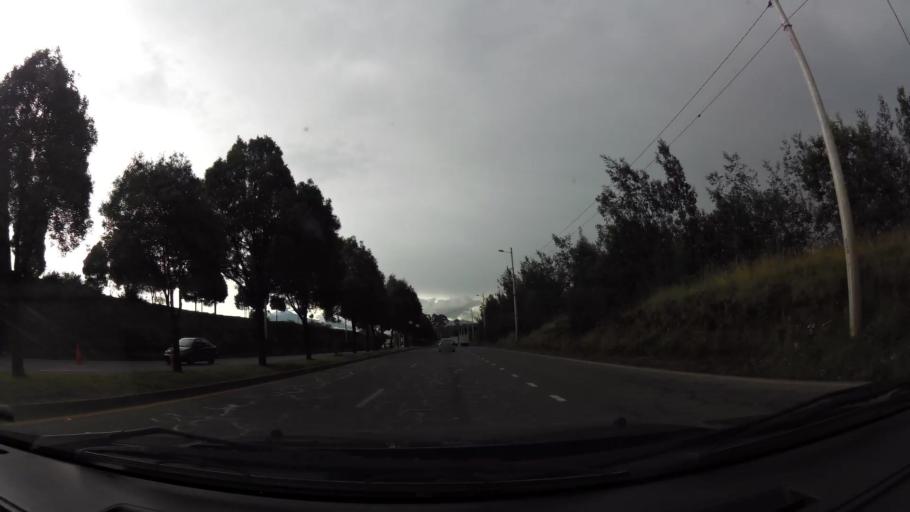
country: EC
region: Pichincha
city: Sangolqui
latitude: -0.3163
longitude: -78.5218
